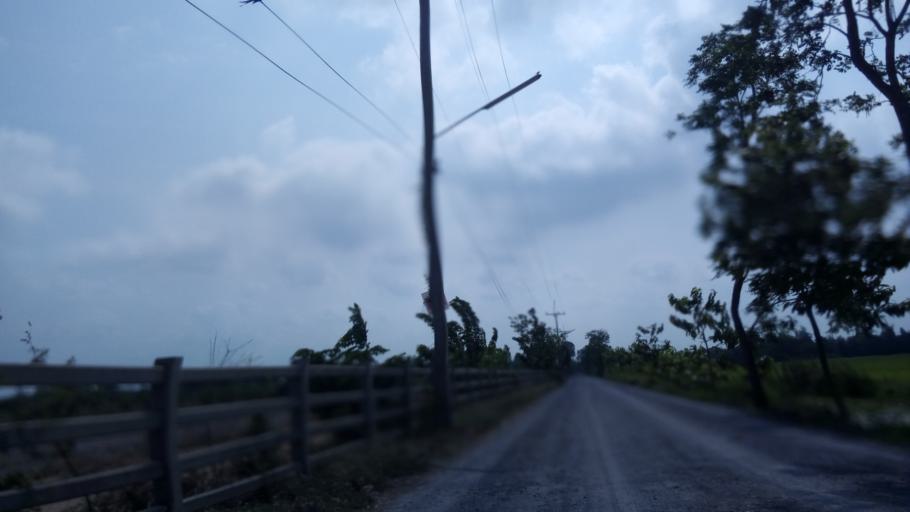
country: TH
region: Pathum Thani
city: Nong Suea
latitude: 14.1886
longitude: 100.8411
